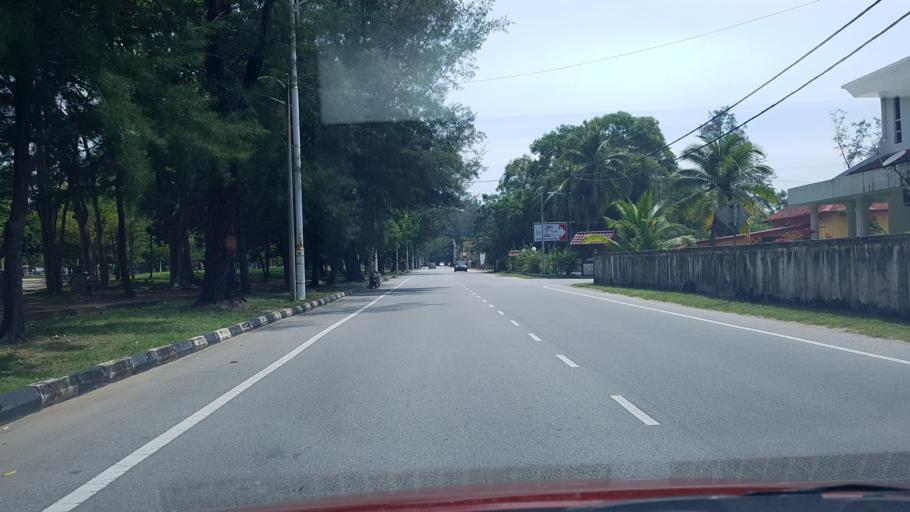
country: MY
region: Terengganu
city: Kuala Terengganu
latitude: 5.3180
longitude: 103.1563
